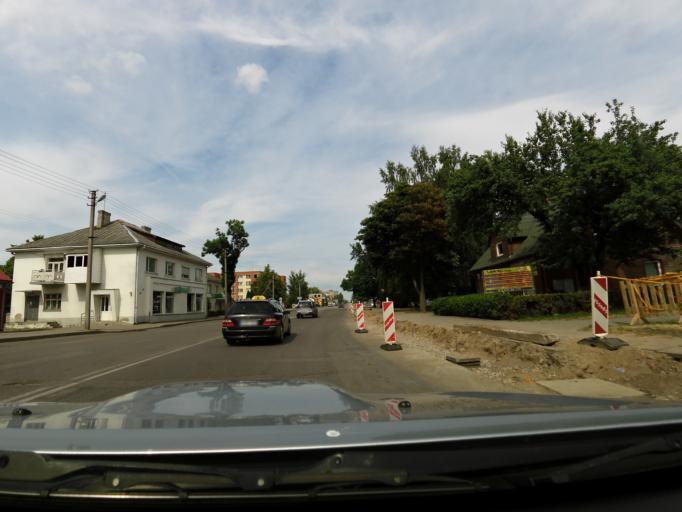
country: LT
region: Marijampoles apskritis
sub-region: Marijampole Municipality
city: Marijampole
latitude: 54.5625
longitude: 23.3538
